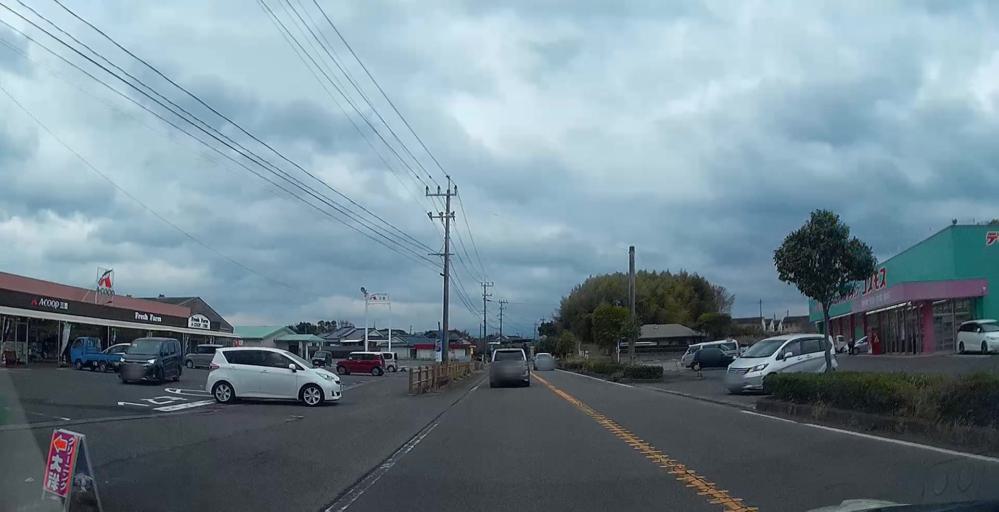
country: JP
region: Kagoshima
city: Akune
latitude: 32.0813
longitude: 130.2029
